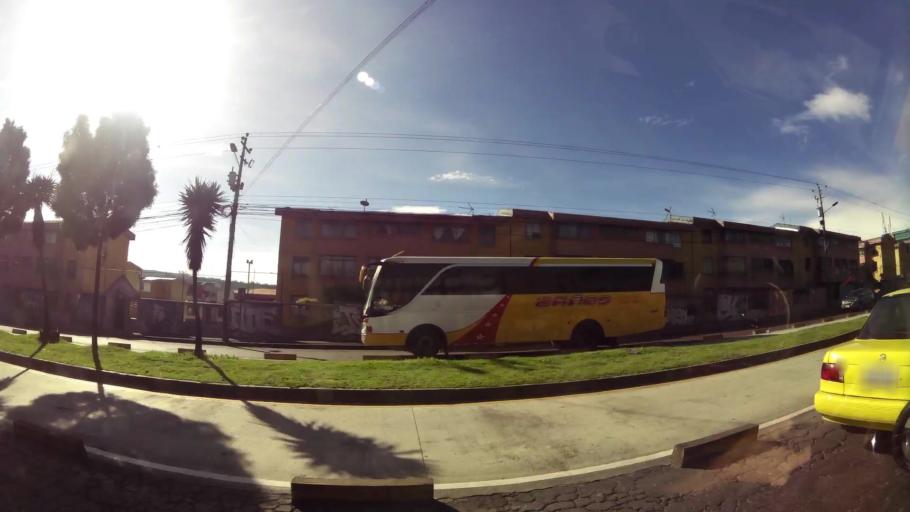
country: EC
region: Pichincha
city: Quito
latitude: -0.3165
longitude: -78.5489
